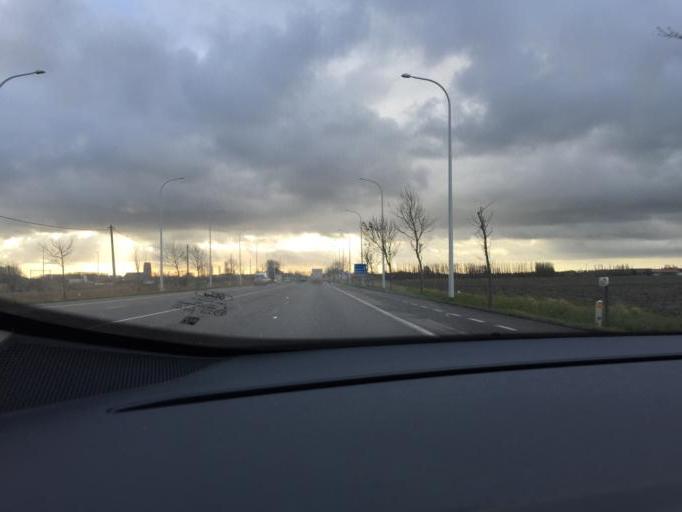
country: BE
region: Flanders
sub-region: Provincie West-Vlaanderen
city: Zeebrugge
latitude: 51.3072
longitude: 3.1890
